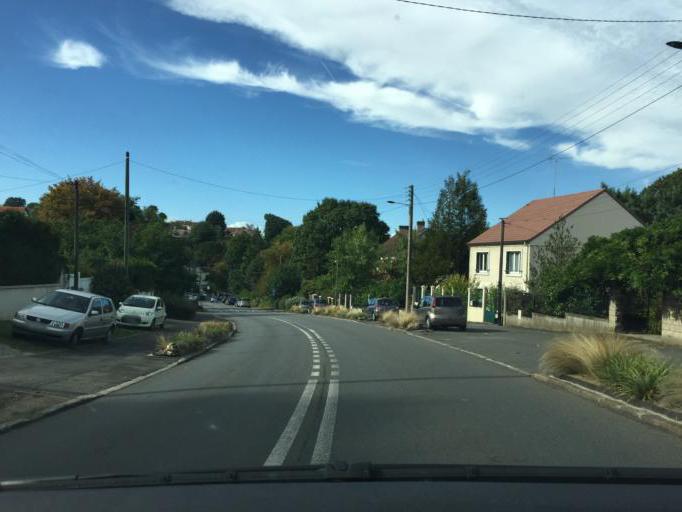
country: FR
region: Ile-de-France
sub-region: Departement de l'Essonne
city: Orsay
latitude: 48.6878
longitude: 2.1840
